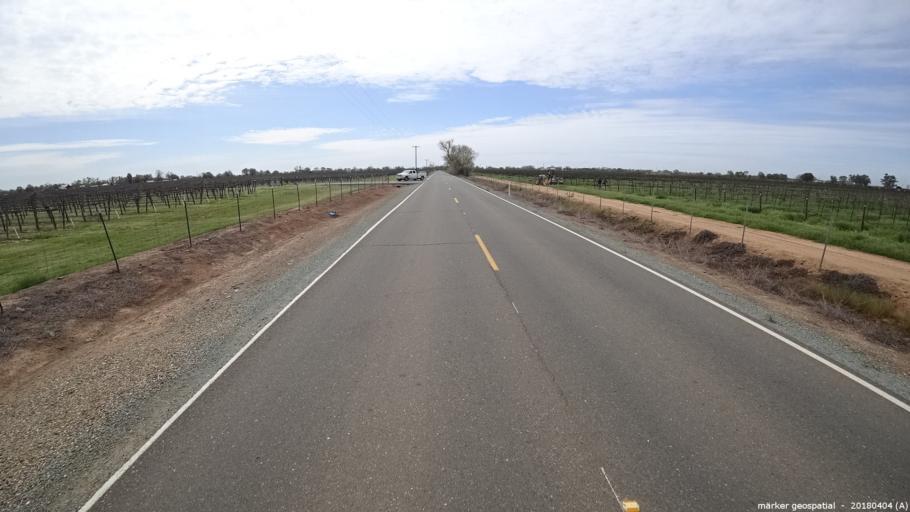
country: US
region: California
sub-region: Sacramento County
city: Clay
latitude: 38.2677
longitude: -121.1714
